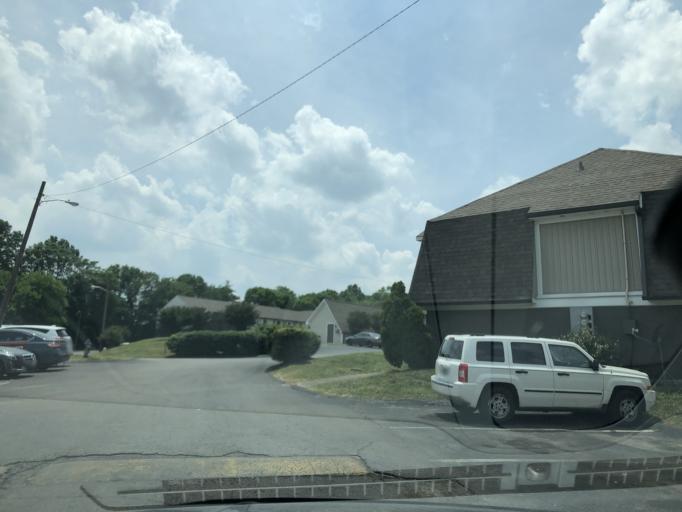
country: US
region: Tennessee
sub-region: Davidson County
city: Oak Hill
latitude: 36.0664
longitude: -86.6896
